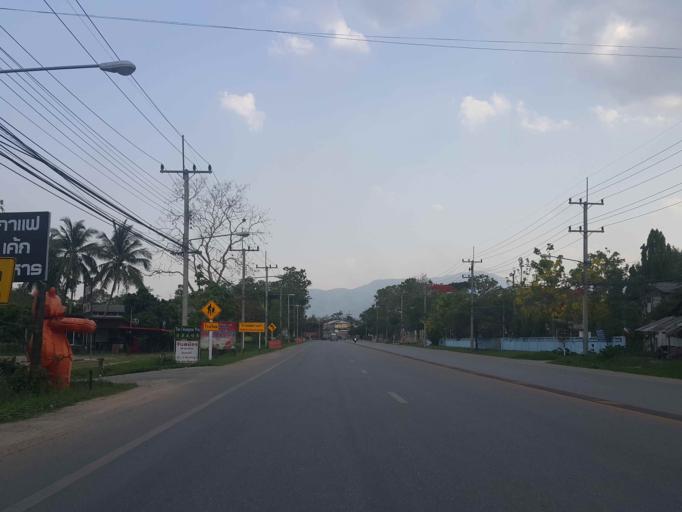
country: TH
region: Chiang Mai
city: San Sai
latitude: 18.9471
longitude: 98.9438
